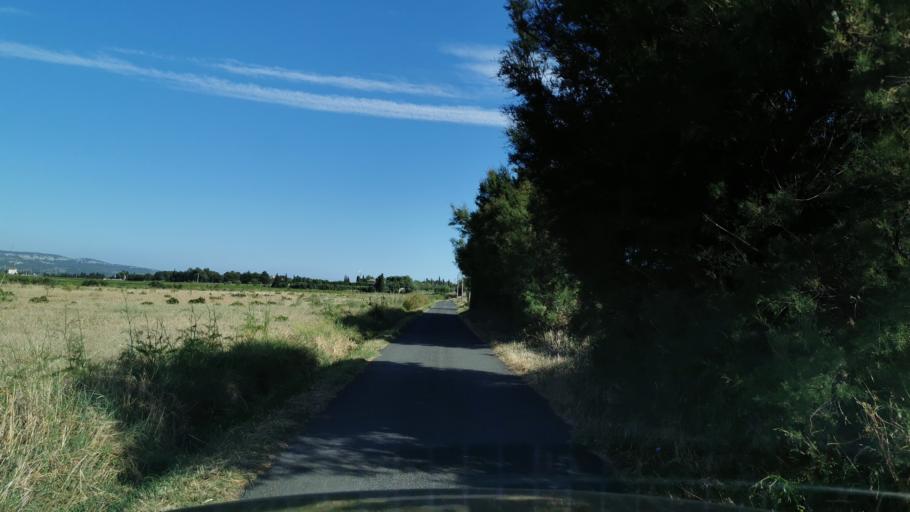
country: FR
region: Languedoc-Roussillon
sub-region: Departement de l'Aude
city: Narbonne
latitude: 43.1628
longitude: 2.9980
